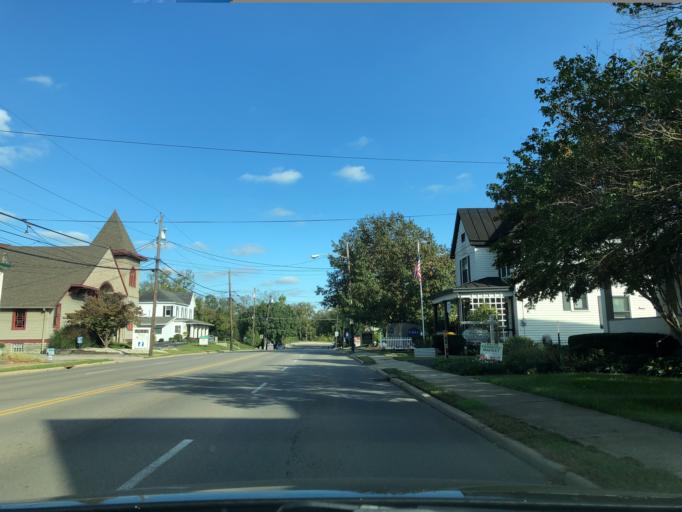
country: US
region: Ohio
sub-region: Hamilton County
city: Loveland
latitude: 39.2689
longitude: -84.2634
